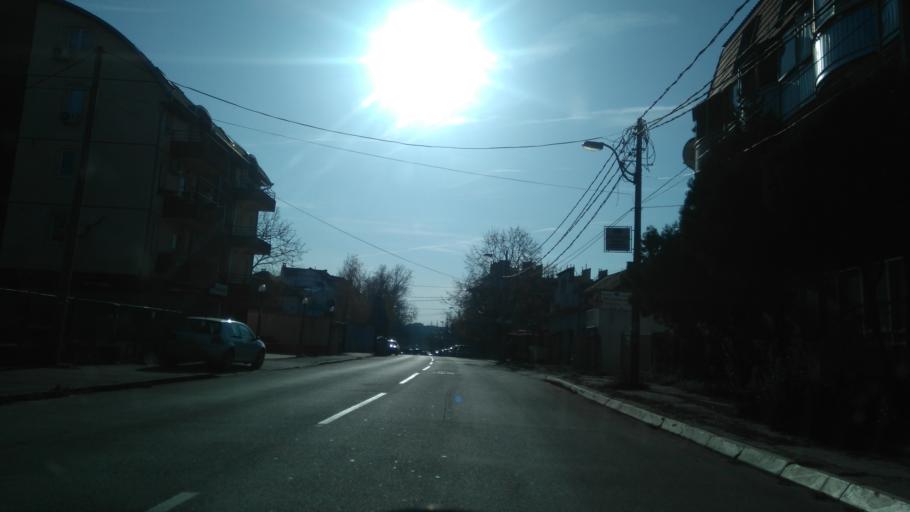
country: RS
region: Central Serbia
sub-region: Belgrade
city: Cukarica
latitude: 44.7571
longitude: 20.4051
